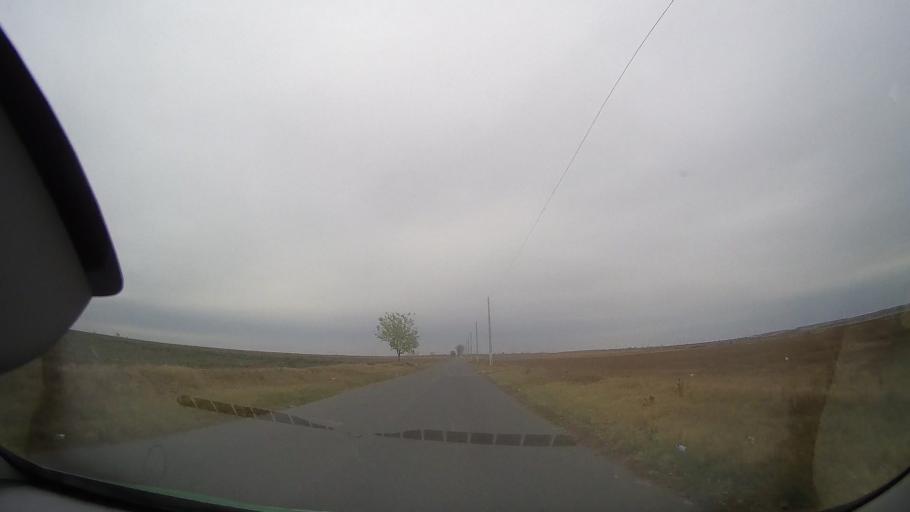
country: RO
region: Braila
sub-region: Comuna Budesti
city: Tataru
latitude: 44.8570
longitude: 27.4233
